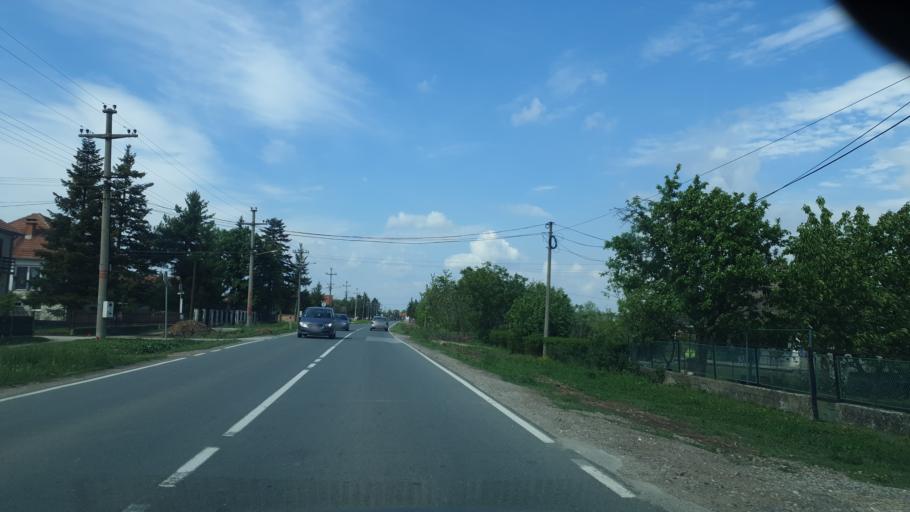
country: RS
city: Zvecka
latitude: 44.6327
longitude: 20.1815
